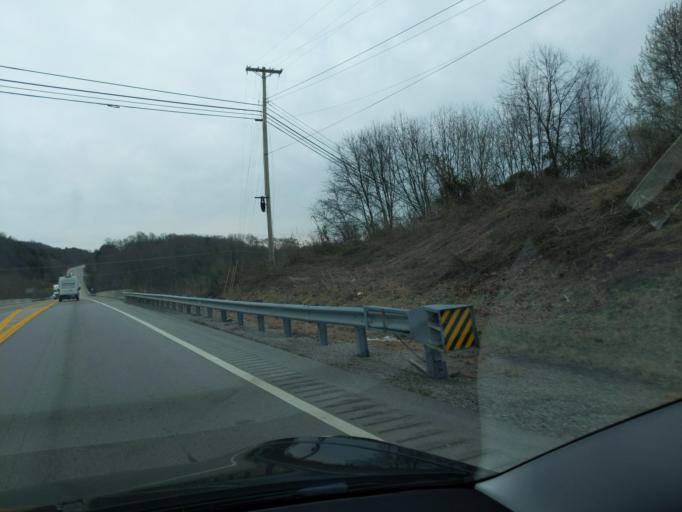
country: US
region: Kentucky
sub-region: Whitley County
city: Corbin
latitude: 36.9165
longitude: -84.0880
